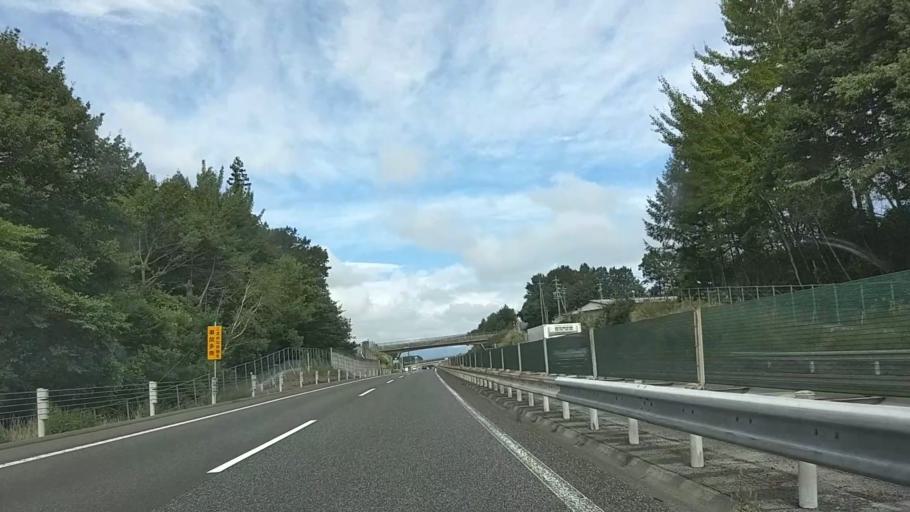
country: JP
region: Nagano
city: Shiojiri
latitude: 36.0927
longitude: 138.0015
